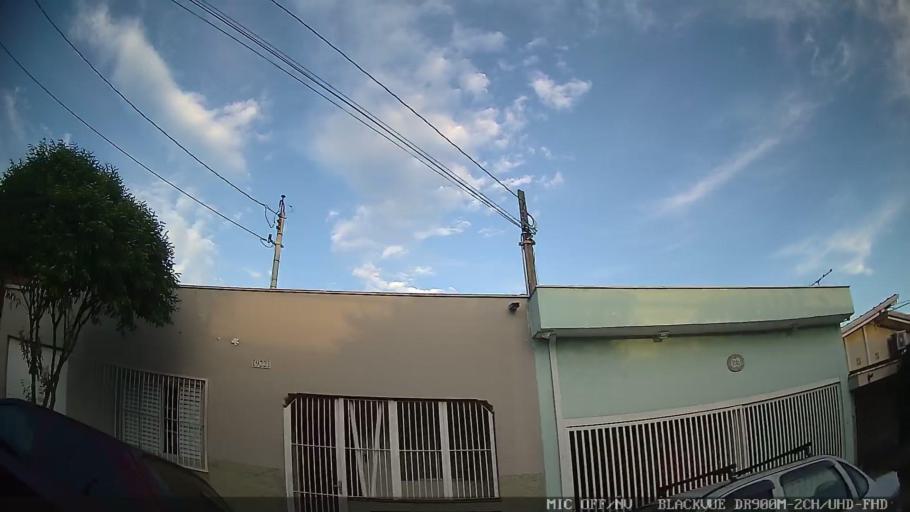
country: BR
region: Sao Paulo
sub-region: Salto
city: Salto
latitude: -23.2018
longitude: -47.2880
